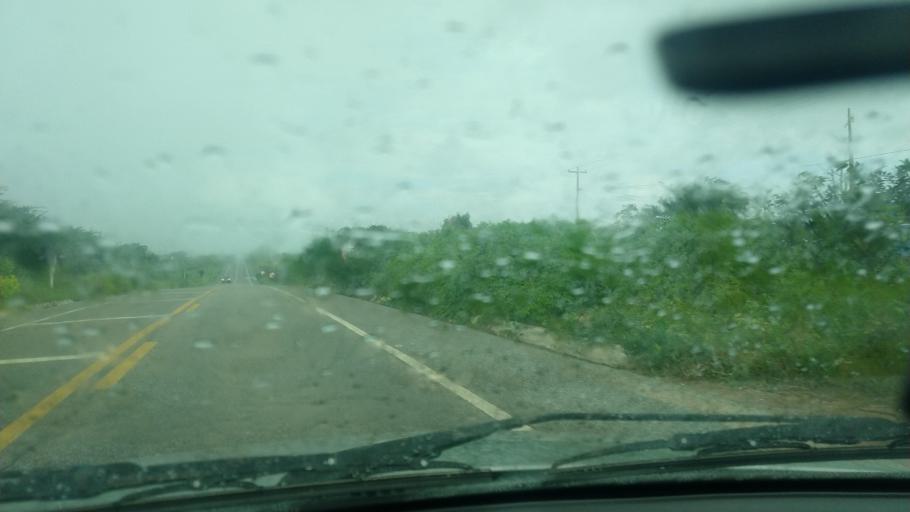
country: BR
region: Rio Grande do Norte
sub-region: Santa Cruz
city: Santa Cruz
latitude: -6.2021
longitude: -36.1951
